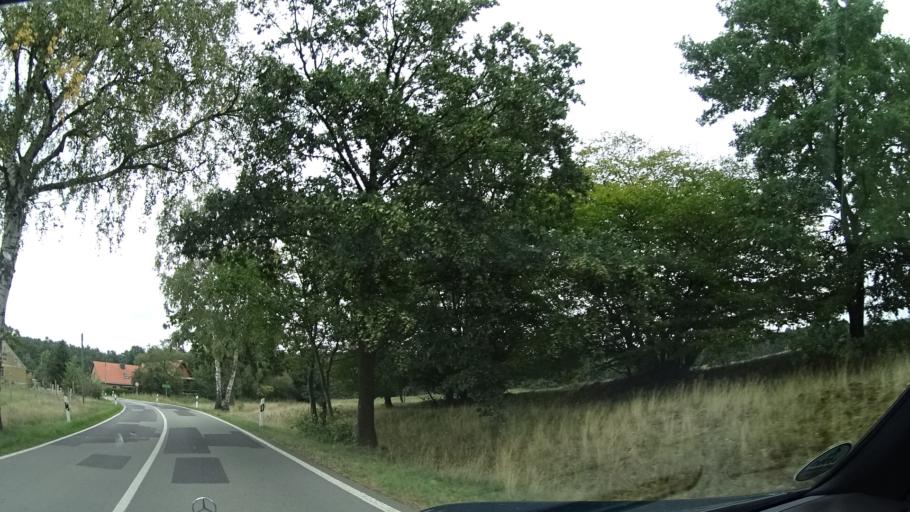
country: DE
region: Brandenburg
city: Walsleben
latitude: 52.9657
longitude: 12.7183
